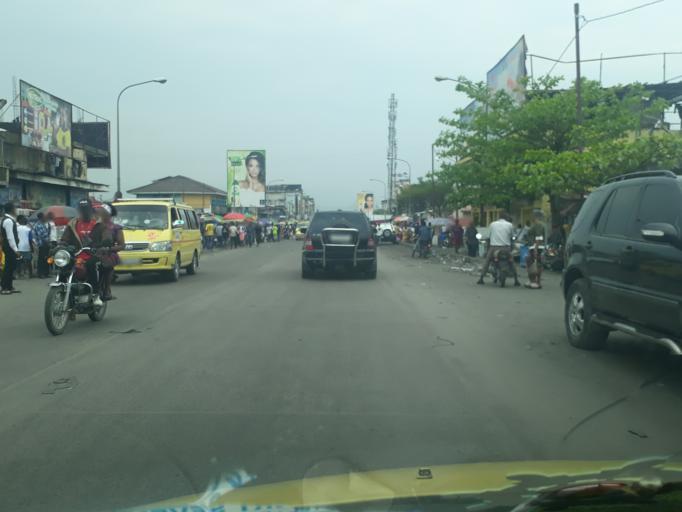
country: CD
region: Kinshasa
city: Kinshasa
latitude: -4.3458
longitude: 15.3122
